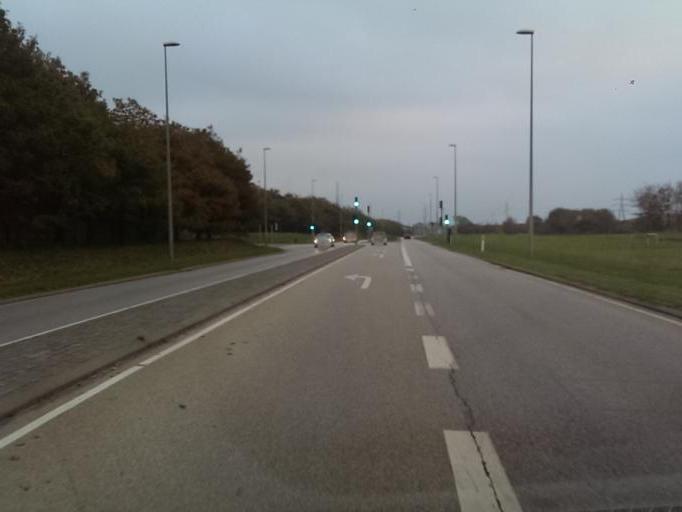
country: DK
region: South Denmark
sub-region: Esbjerg Kommune
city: Esbjerg
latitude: 55.4626
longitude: 8.4710
